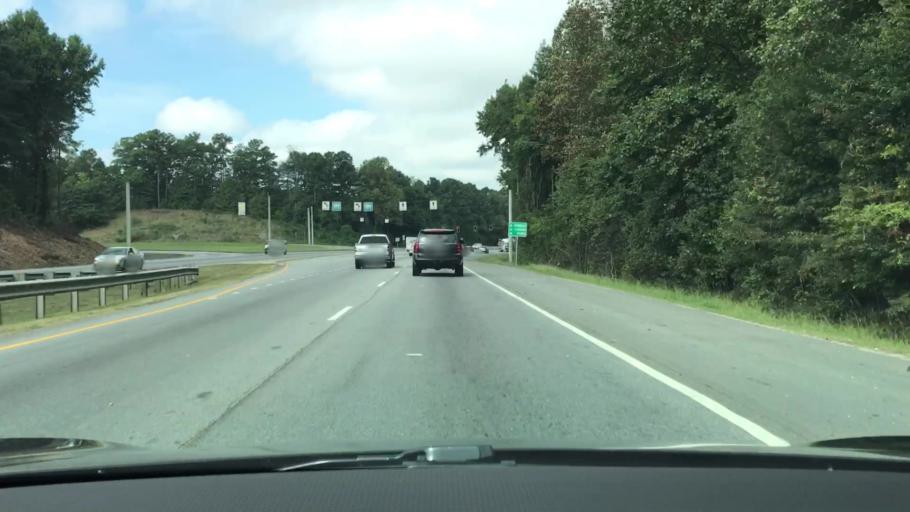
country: US
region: Georgia
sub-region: Hall County
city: Gainesville
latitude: 34.2854
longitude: -83.8067
